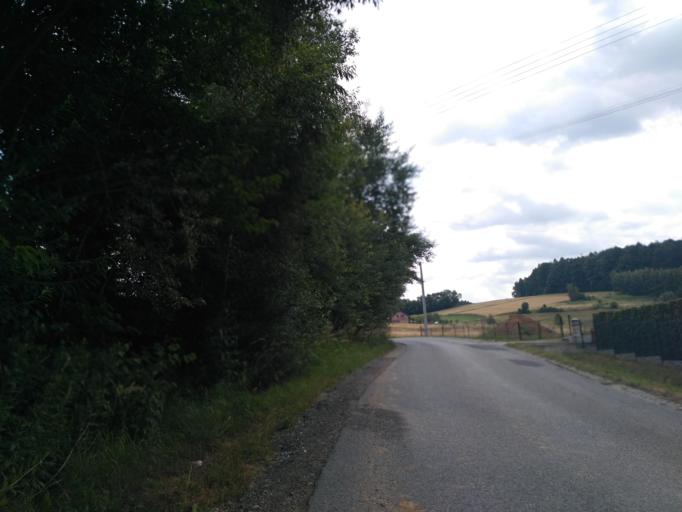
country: PL
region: Subcarpathian Voivodeship
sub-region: Powiat ropczycko-sedziszowski
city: Niedzwiada
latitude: 50.0364
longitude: 21.5030
